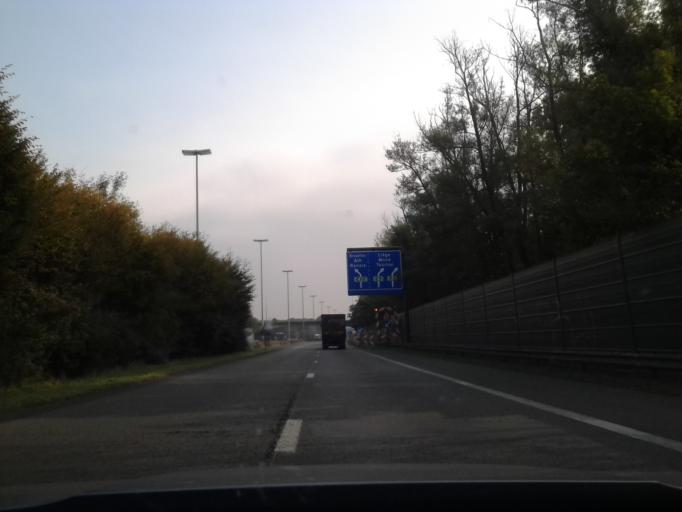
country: BE
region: Wallonia
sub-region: Province du Hainaut
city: Tournai
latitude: 50.6346
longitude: 3.3853
